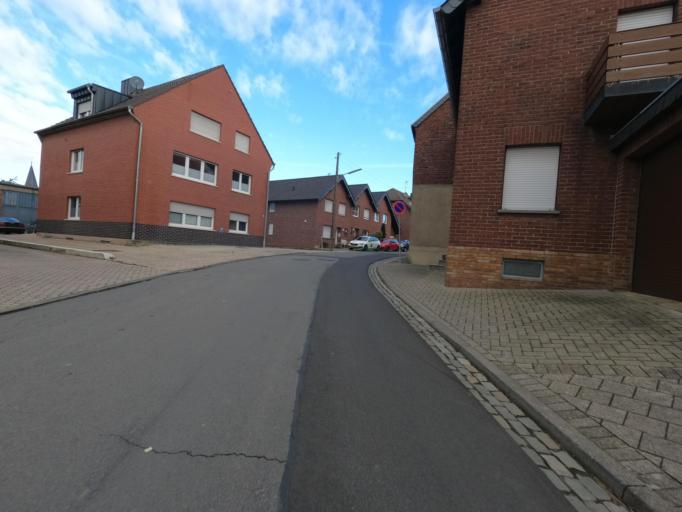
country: DE
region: North Rhine-Westphalia
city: Huckelhoven
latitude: 51.0488
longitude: 6.2490
